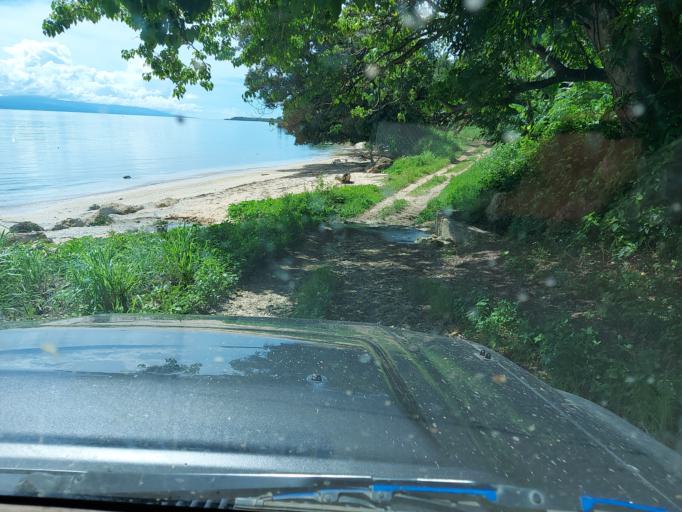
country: VU
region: Malampa
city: Lakatoro
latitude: -16.3286
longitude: 167.7288
